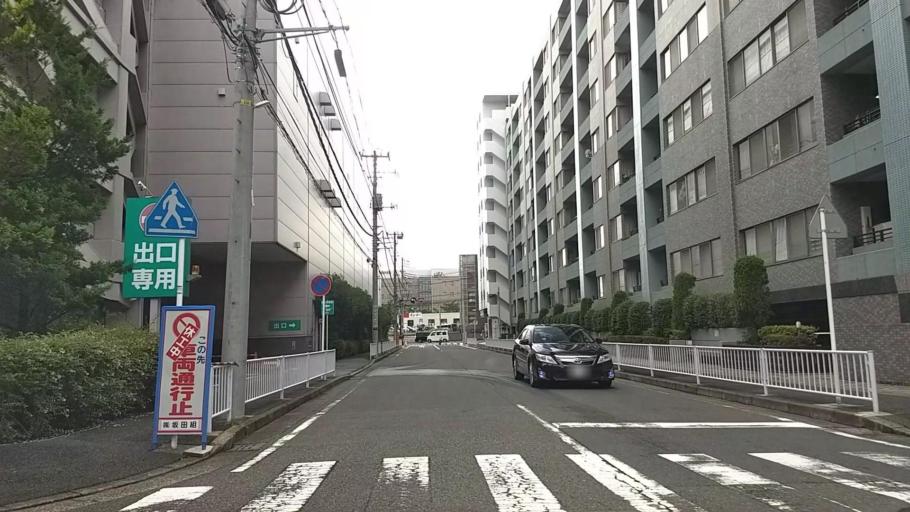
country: JP
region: Kanagawa
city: Yokohama
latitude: 35.5031
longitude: 139.6088
